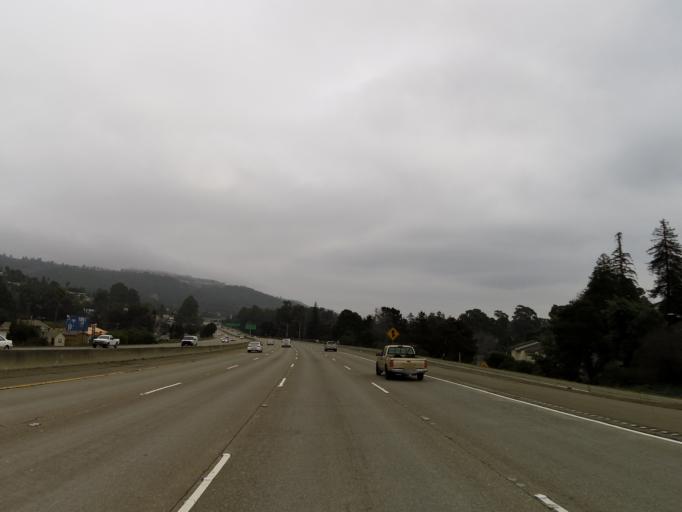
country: US
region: California
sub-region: Alameda County
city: Alameda
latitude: 37.7847
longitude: -122.1910
